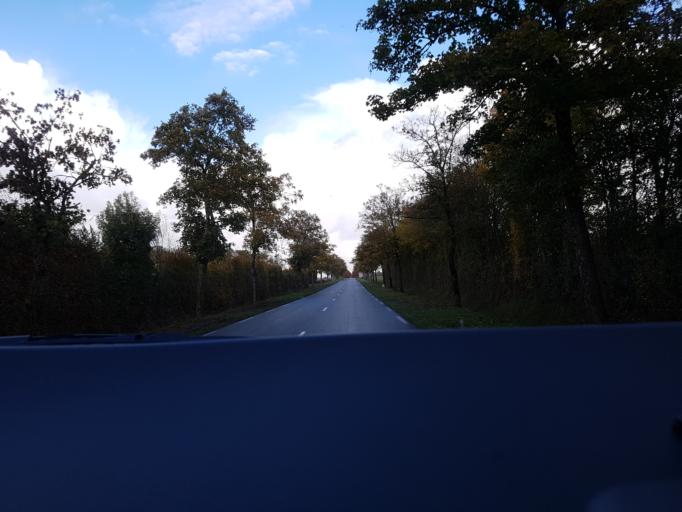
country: FR
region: Poitou-Charentes
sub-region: Departement des Deux-Sevres
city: Brioux-sur-Boutonne
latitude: 46.0887
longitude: -0.2899
